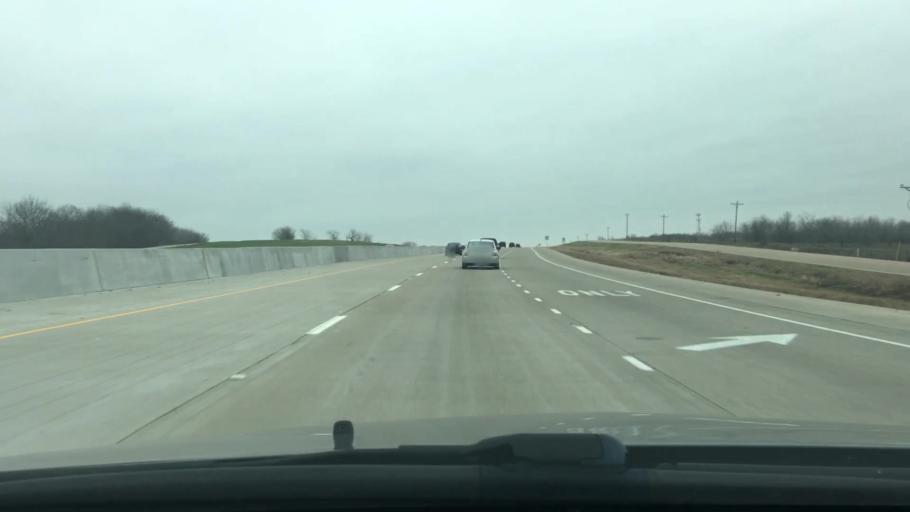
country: US
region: Texas
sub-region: Freestone County
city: Wortham
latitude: 31.8882
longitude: -96.3535
